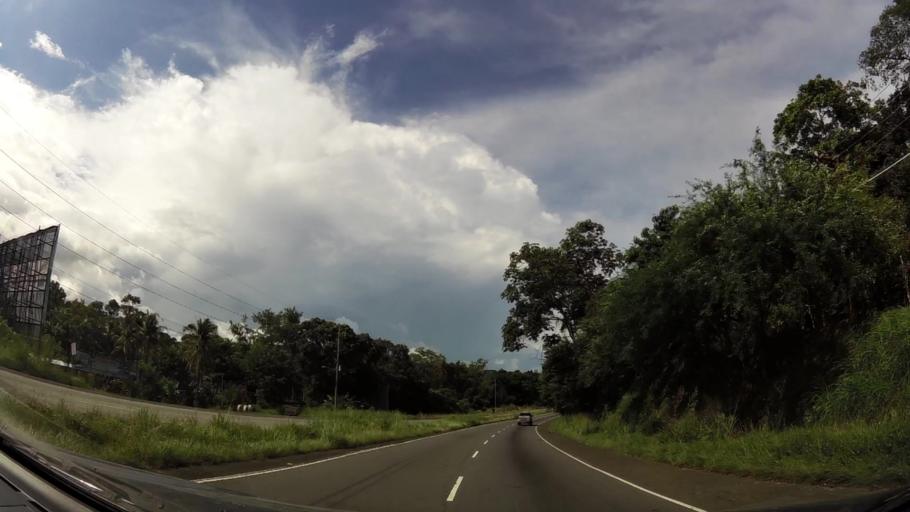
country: PA
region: Panama
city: Capira
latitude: 8.7214
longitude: -79.8856
